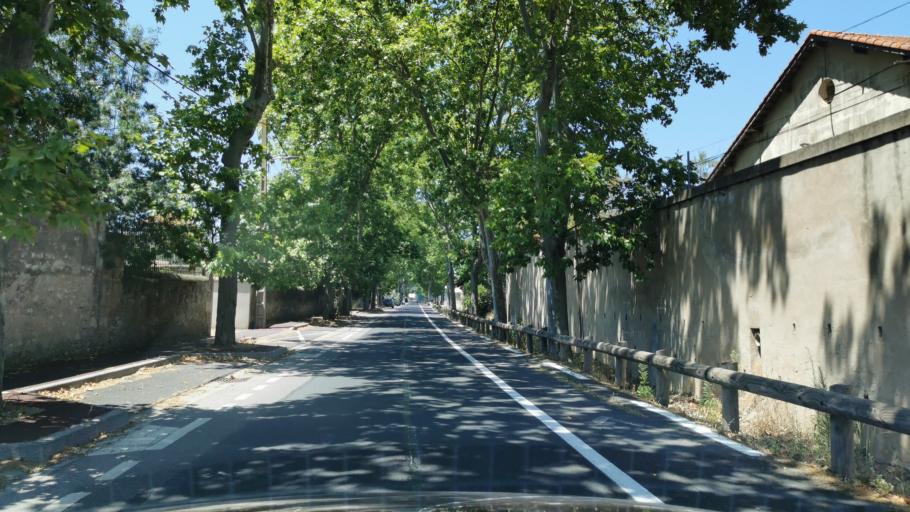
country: FR
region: Languedoc-Roussillon
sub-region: Departement de l'Herault
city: Beziers
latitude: 43.3393
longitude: 3.1959
